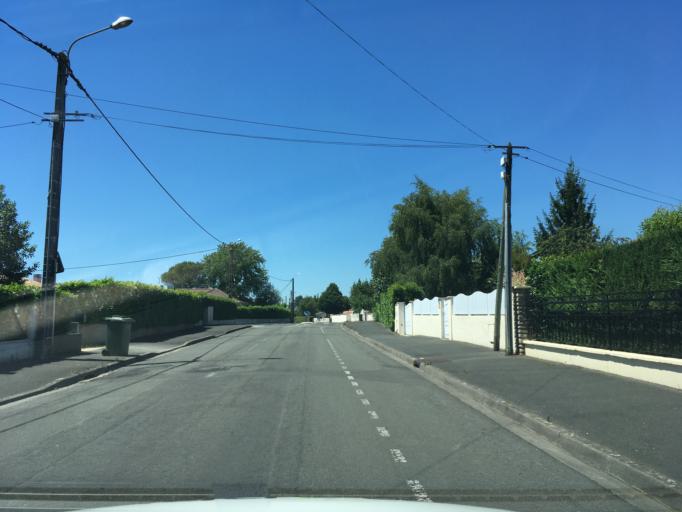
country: FR
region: Poitou-Charentes
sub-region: Departement des Deux-Sevres
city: Niort
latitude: 46.3410
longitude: -0.4395
